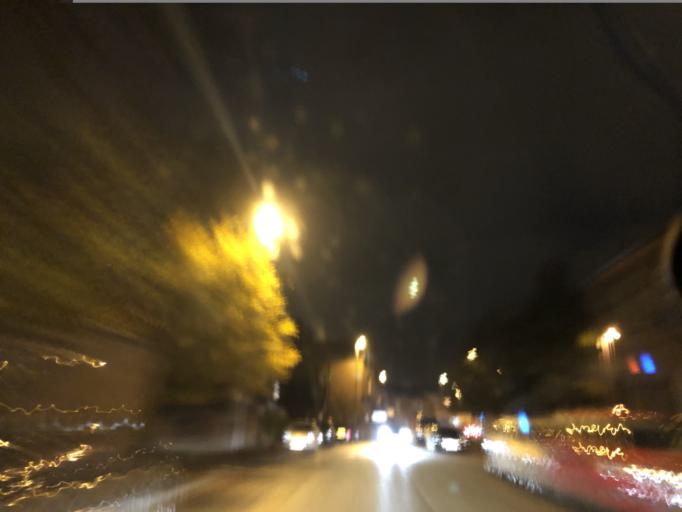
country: GB
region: England
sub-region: Borough of Oldham
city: Oldham
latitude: 53.5256
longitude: -2.1122
